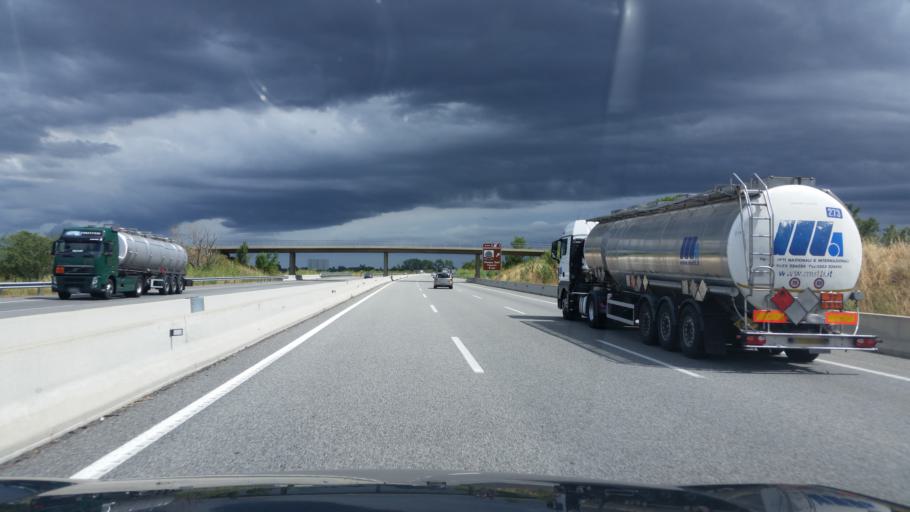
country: ES
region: Catalonia
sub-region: Provincia de Girona
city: Pont de Molins
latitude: 42.3339
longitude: 2.9288
